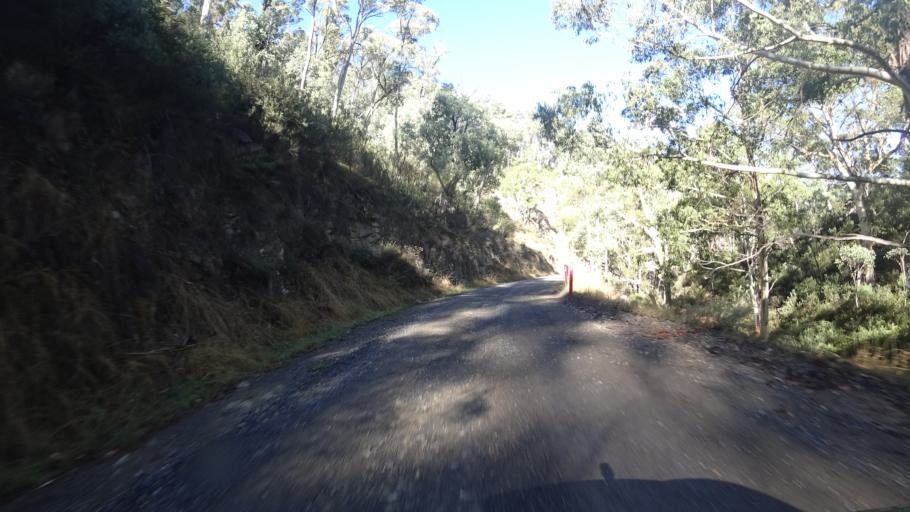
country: AU
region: New South Wales
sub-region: Tumut Shire
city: Tumut
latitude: -35.7253
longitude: 148.5006
